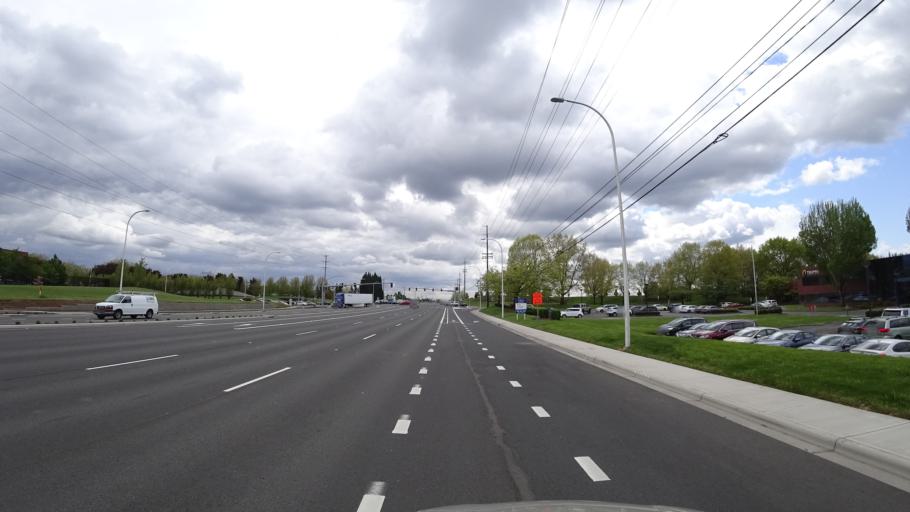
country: US
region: Oregon
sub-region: Washington County
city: Rockcreek
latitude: 45.5476
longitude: -122.9001
